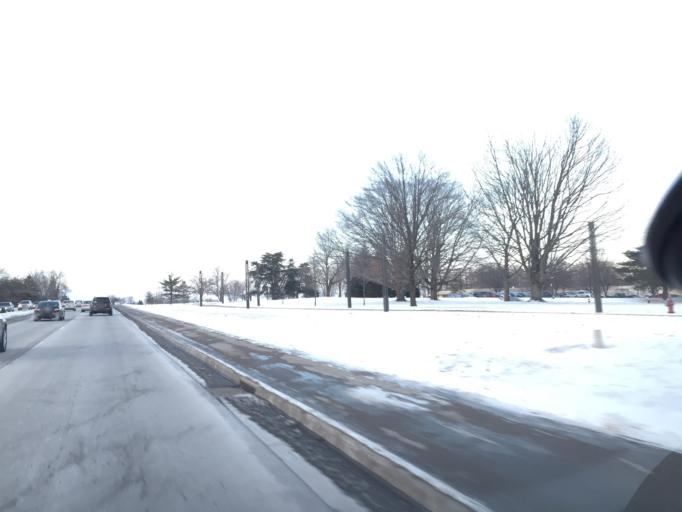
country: US
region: Indiana
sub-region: Monroe County
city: Bloomington
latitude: 39.1725
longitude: -86.5027
